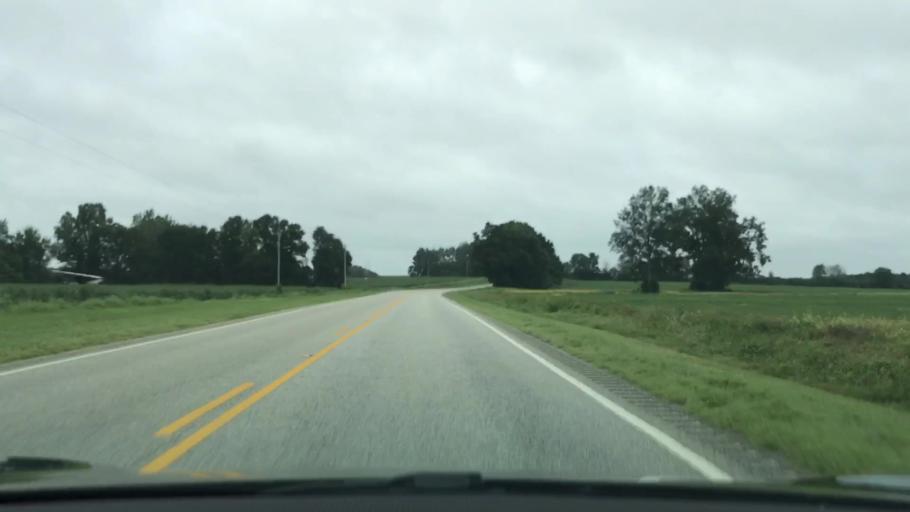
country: US
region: Alabama
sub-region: Coffee County
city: Elba
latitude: 31.3183
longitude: -86.1343
